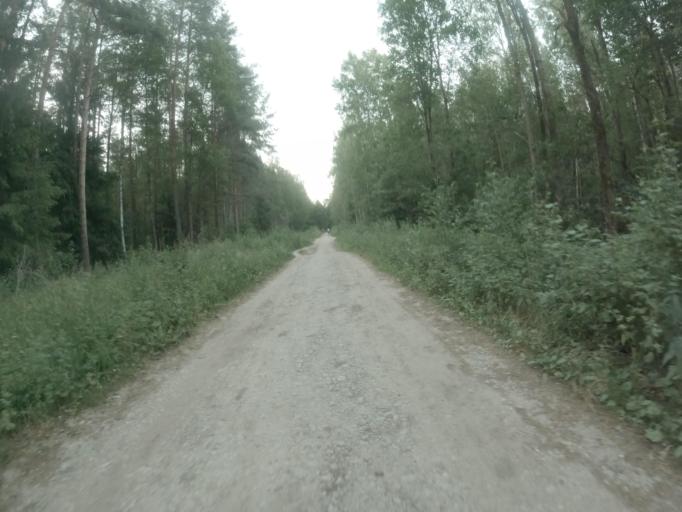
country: RU
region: St.-Petersburg
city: Krasnogvargeisky
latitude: 59.9560
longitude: 30.5208
